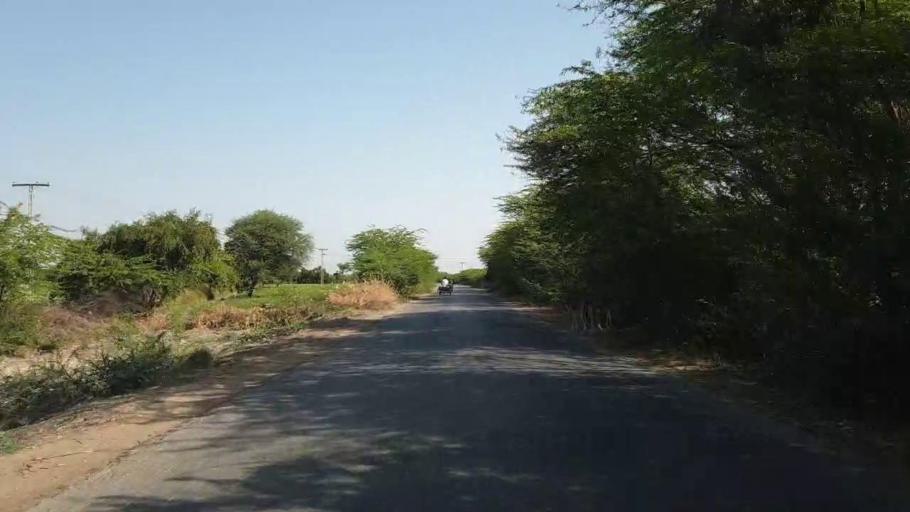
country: PK
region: Sindh
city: Chor
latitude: 25.4854
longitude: 69.7802
